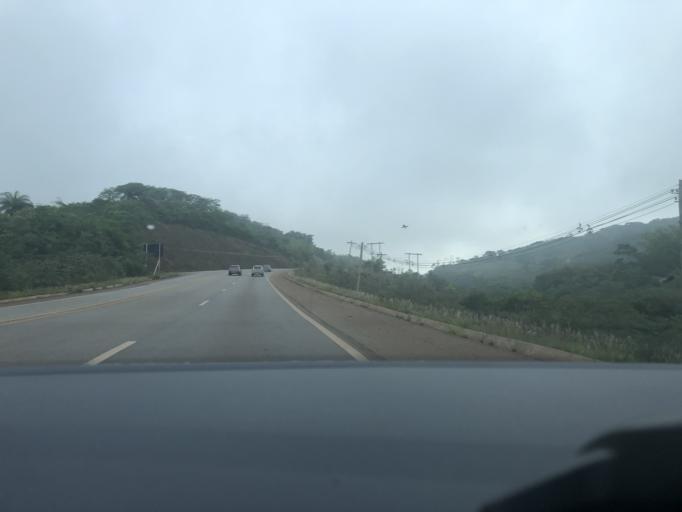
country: BR
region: Minas Gerais
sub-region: Congonhas
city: Congonhas
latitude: -20.5972
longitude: -43.9383
